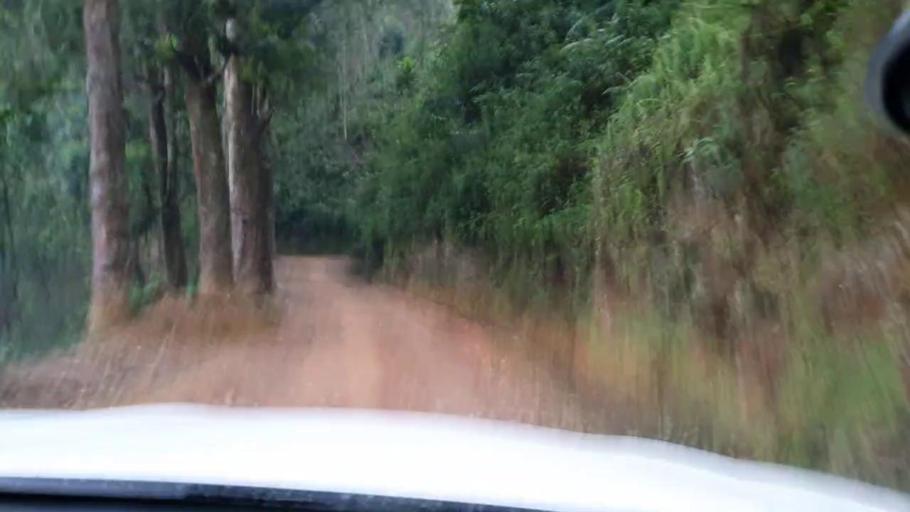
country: RW
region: Western Province
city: Cyangugu
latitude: -2.4112
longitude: 29.1952
